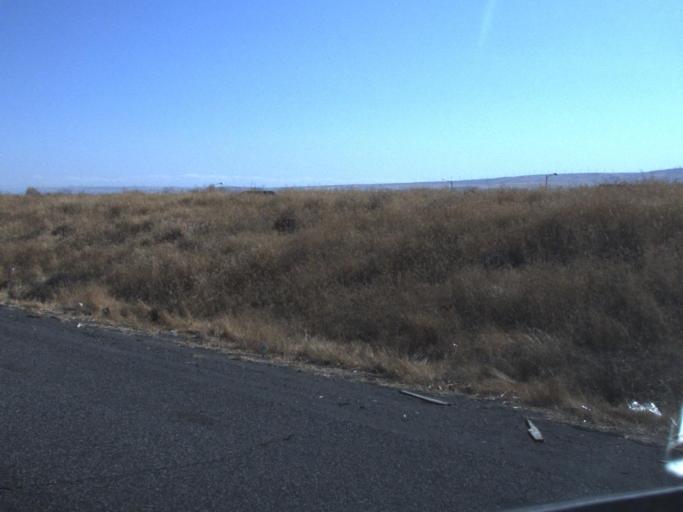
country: US
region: Washington
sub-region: Franklin County
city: West Pasco
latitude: 46.2607
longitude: -119.1667
